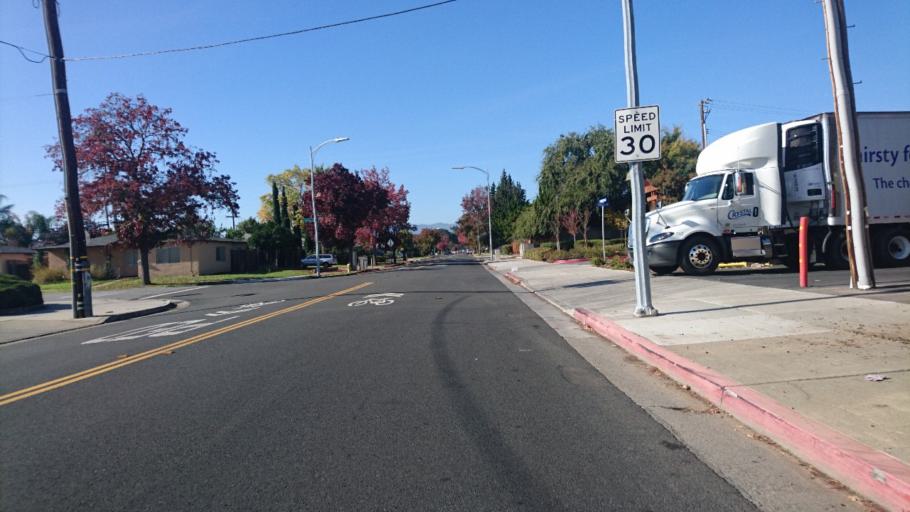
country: US
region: California
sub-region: Santa Clara County
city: Cambrian Park
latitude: 37.2703
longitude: -121.9075
